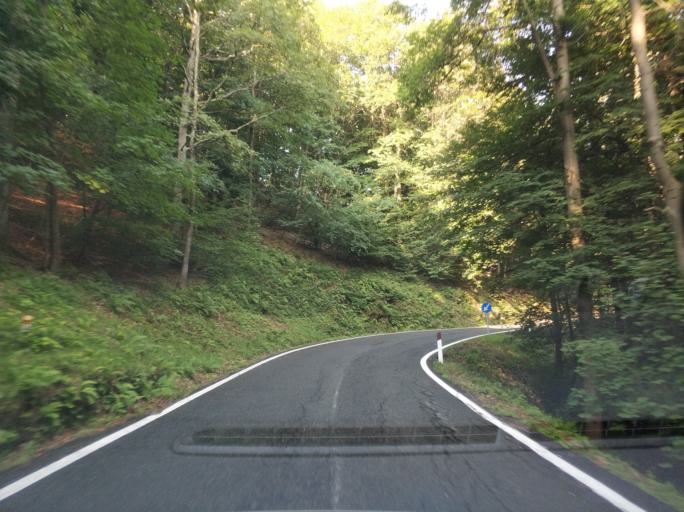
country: IT
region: Piedmont
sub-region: Provincia di Torino
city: Viu
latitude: 45.2234
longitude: 7.3884
